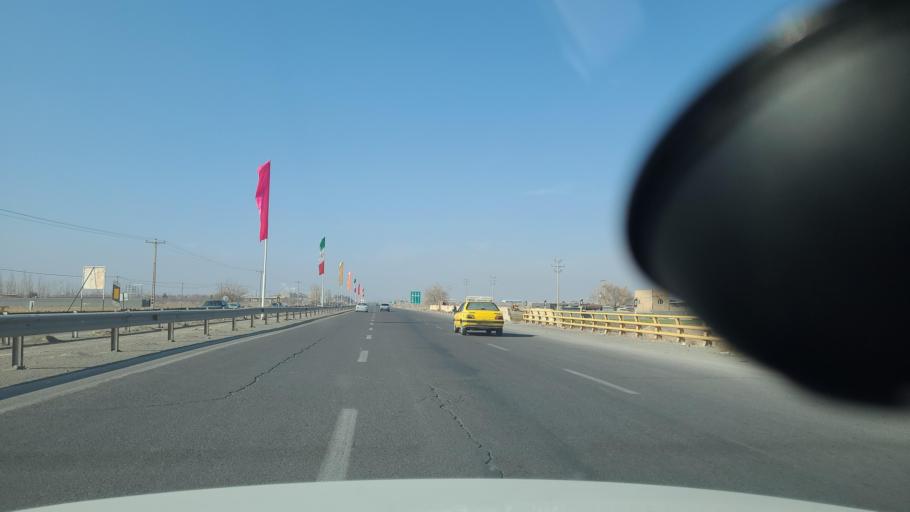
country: IR
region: Razavi Khorasan
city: Fariman
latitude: 35.7081
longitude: 59.8335
